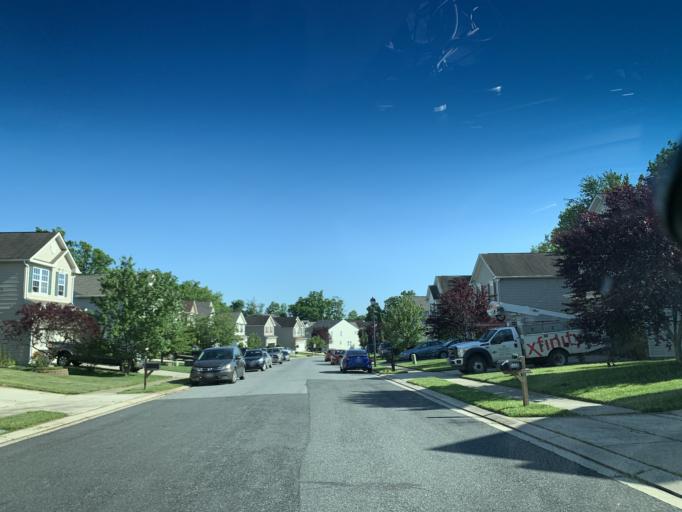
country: US
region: Maryland
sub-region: Harford County
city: Riverside
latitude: 39.4825
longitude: -76.2372
